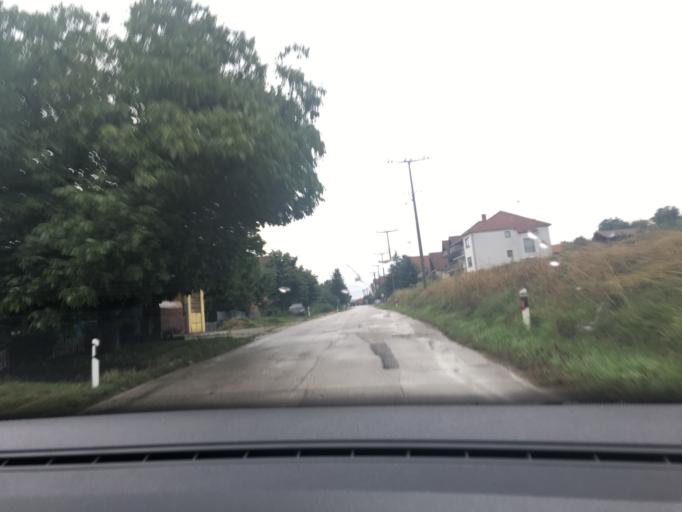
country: RS
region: Central Serbia
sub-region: Nisavski Okrug
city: Aleksinac
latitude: 43.5544
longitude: 21.7054
